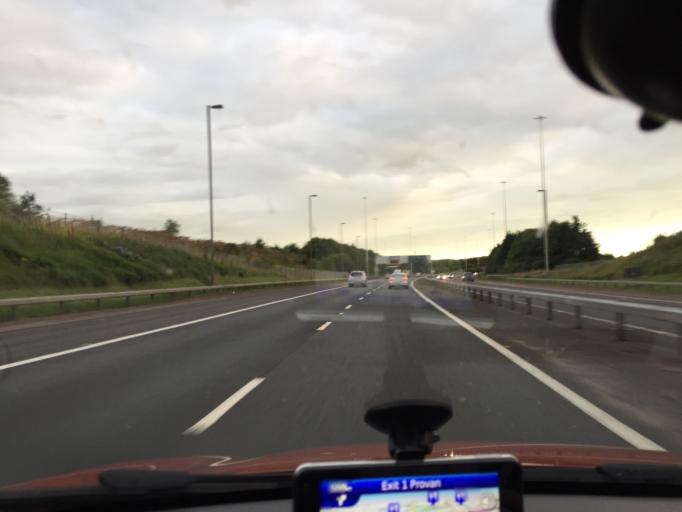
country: GB
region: Scotland
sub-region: East Dunbartonshire
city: Bishopbriggs
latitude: 55.8773
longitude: -4.1980
